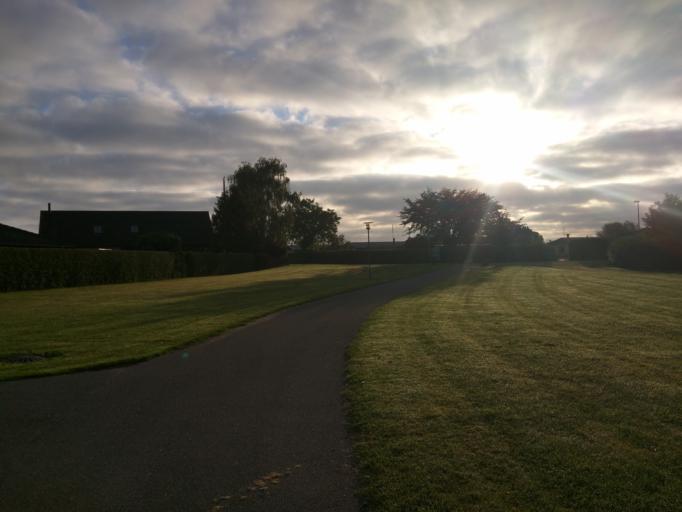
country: DK
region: Central Jutland
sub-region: Viborg Kommune
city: Viborg
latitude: 56.4724
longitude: 9.3877
